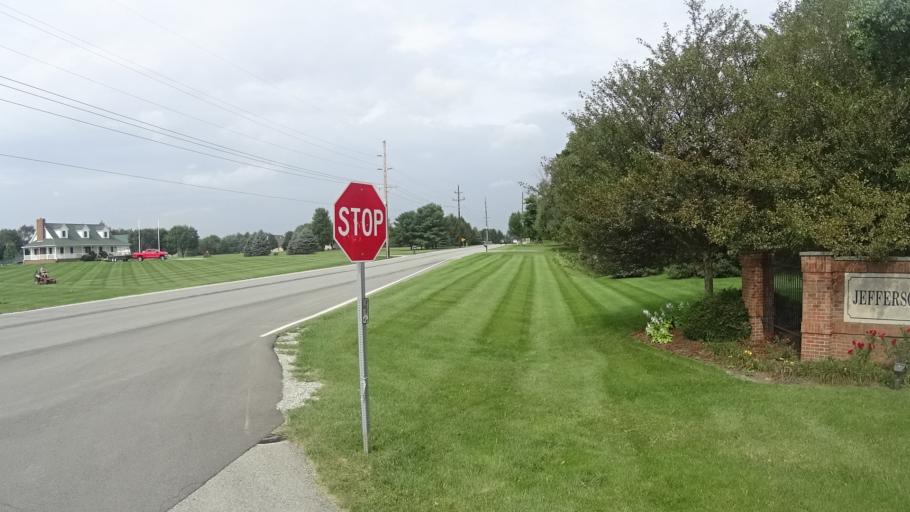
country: US
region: Indiana
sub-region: Madison County
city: Pendleton
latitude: 40.0098
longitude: -85.7954
